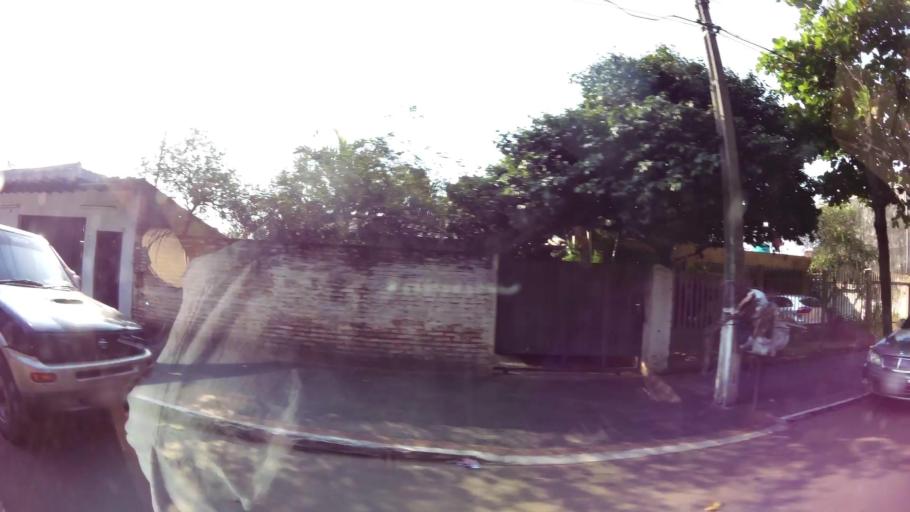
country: PY
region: Central
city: Lambare
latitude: -25.3455
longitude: -57.5824
